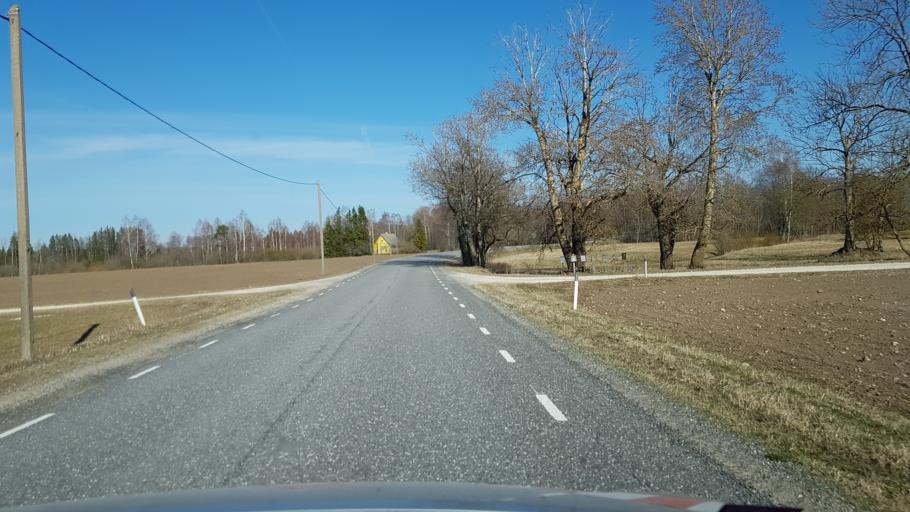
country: EE
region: Jaervamaa
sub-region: Koeru vald
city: Koeru
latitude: 59.0078
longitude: 26.1042
